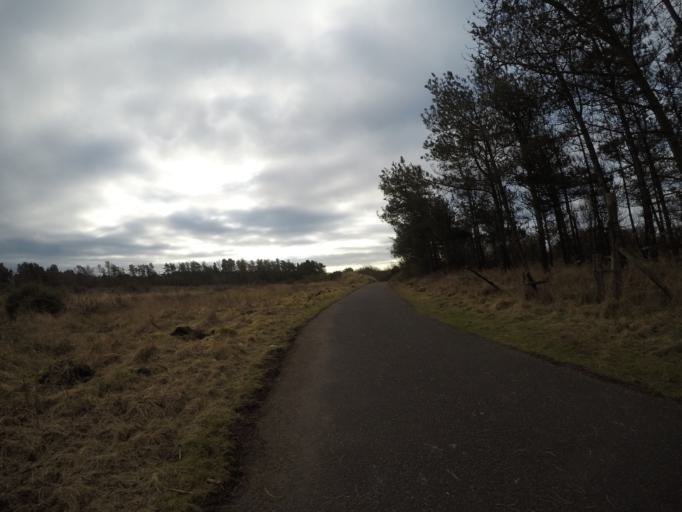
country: GB
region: Scotland
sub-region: North Ayrshire
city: Irvine
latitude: 55.5933
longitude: -4.6714
